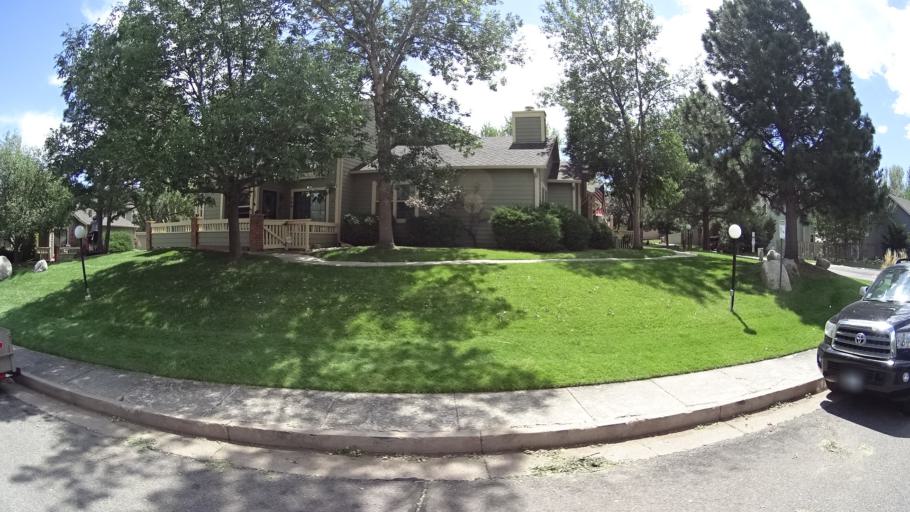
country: US
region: Colorado
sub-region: El Paso County
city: Stratmoor
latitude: 38.7717
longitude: -104.8154
